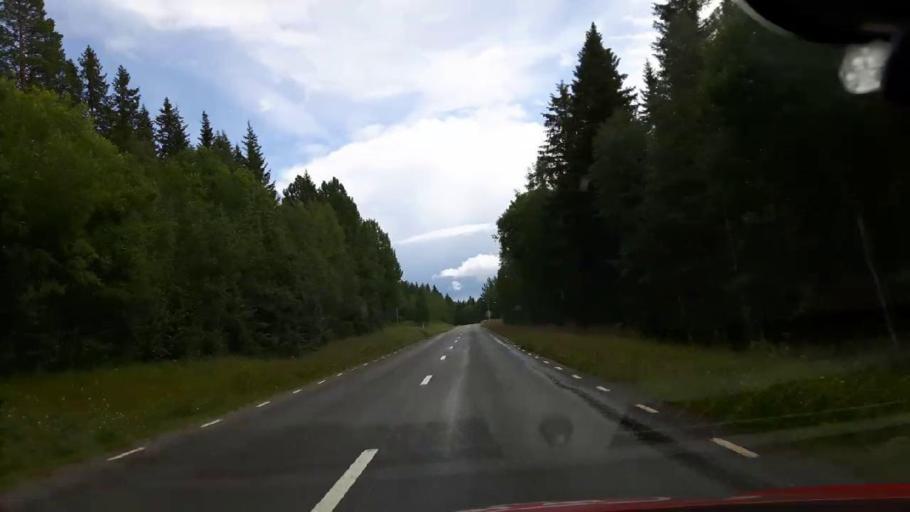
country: SE
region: Jaemtland
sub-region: Stroemsunds Kommun
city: Stroemsund
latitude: 64.3401
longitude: 14.9512
